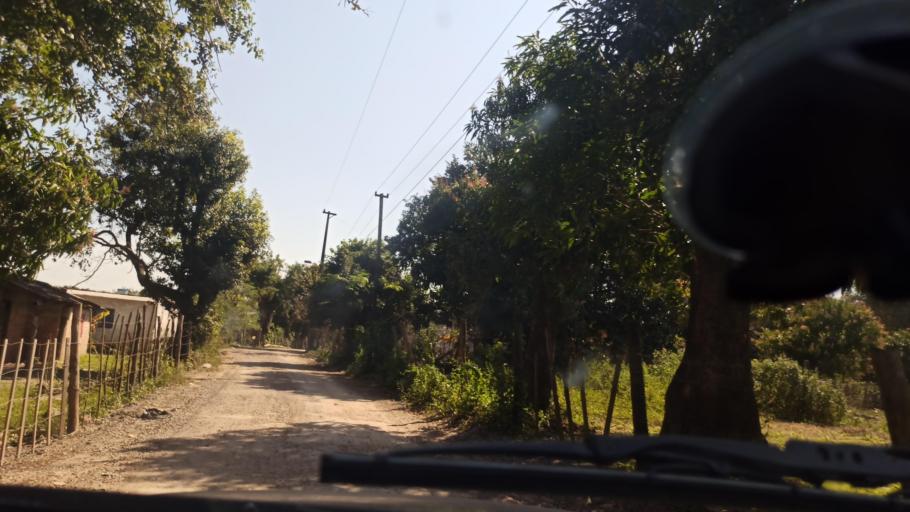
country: AR
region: Formosa
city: Clorinda
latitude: -25.3007
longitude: -57.7044
